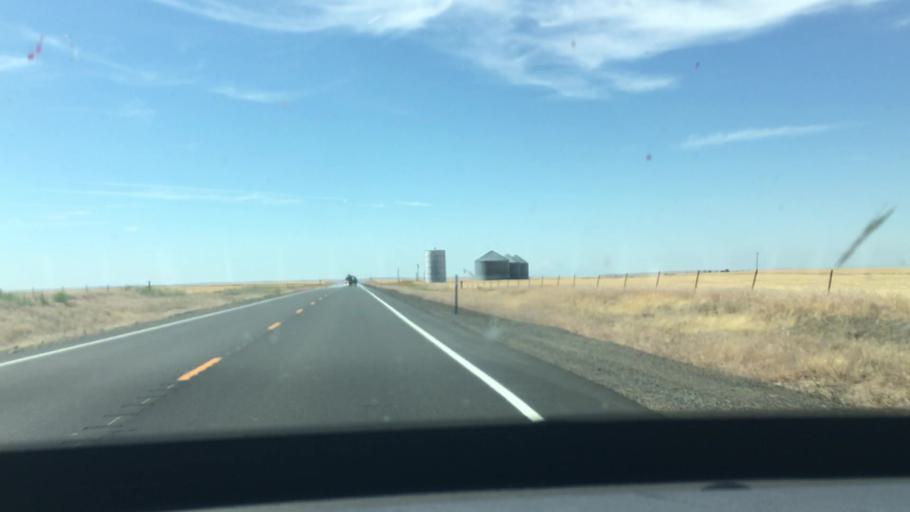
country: US
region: Oregon
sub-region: Sherman County
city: Moro
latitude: 45.2982
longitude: -120.7587
